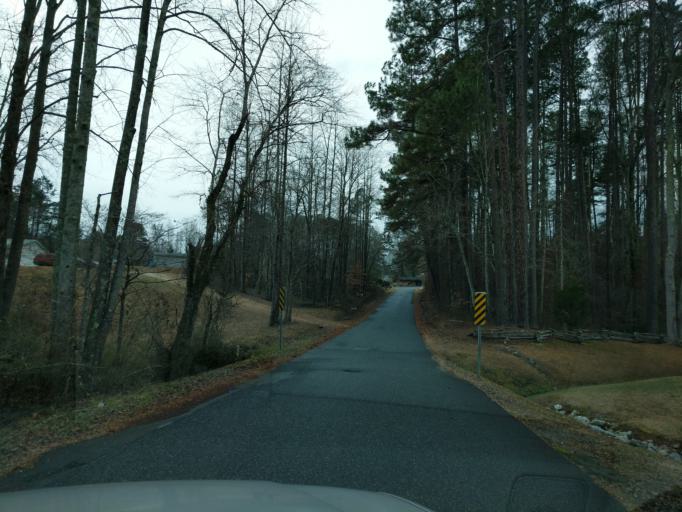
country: US
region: South Carolina
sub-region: Oconee County
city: Walhalla
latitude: 34.7833
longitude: -83.1069
